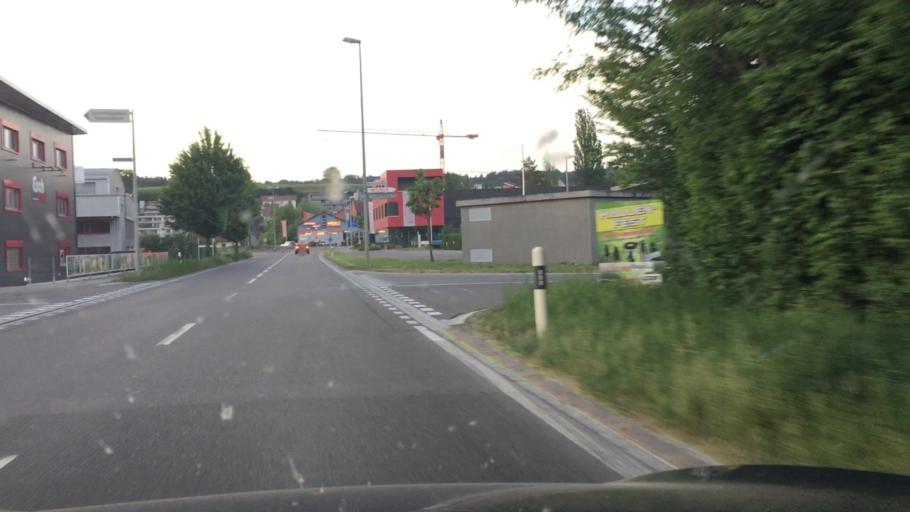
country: CH
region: Thurgau
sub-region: Frauenfeld District
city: Mullheim
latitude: 47.5982
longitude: 8.9960
